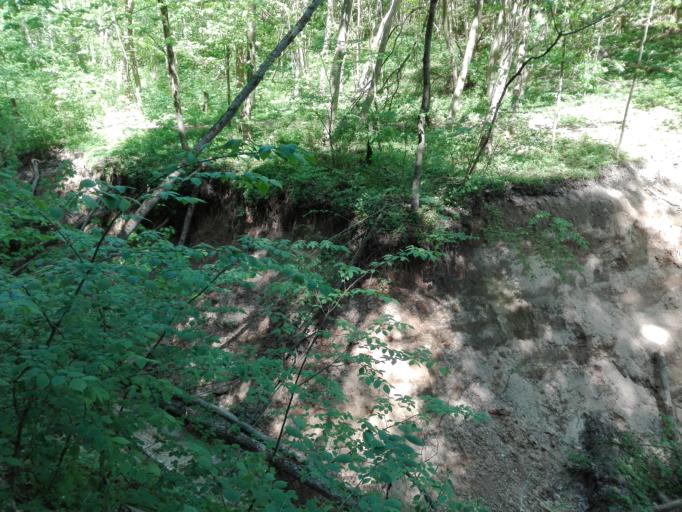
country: LT
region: Vilnius County
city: Lazdynai
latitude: 54.6886
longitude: 25.2233
